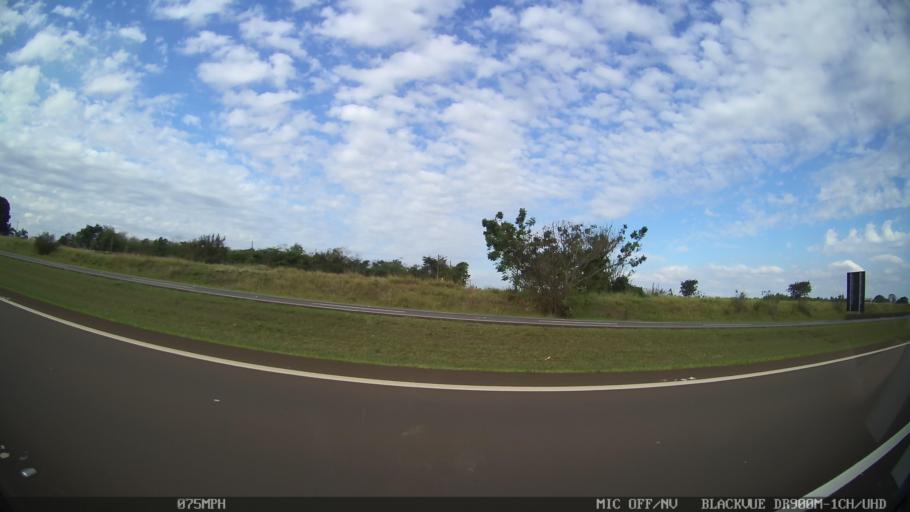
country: BR
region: Sao Paulo
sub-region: Iracemapolis
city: Iracemapolis
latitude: -22.6044
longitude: -47.4579
